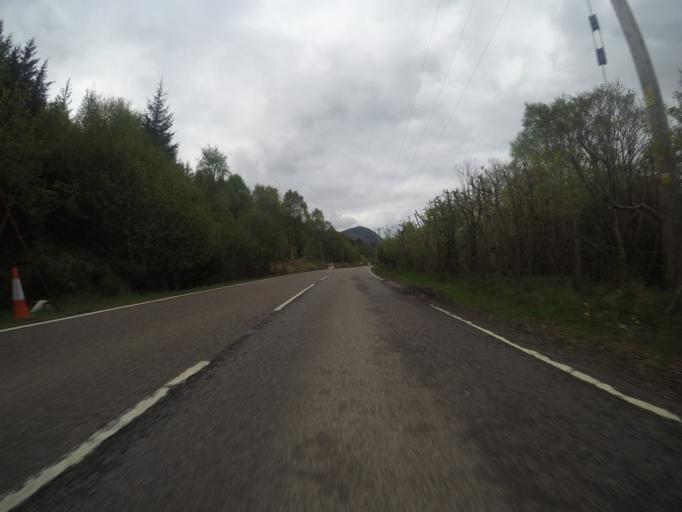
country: GB
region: Scotland
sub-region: Highland
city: Beauly
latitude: 57.1967
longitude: -4.6122
